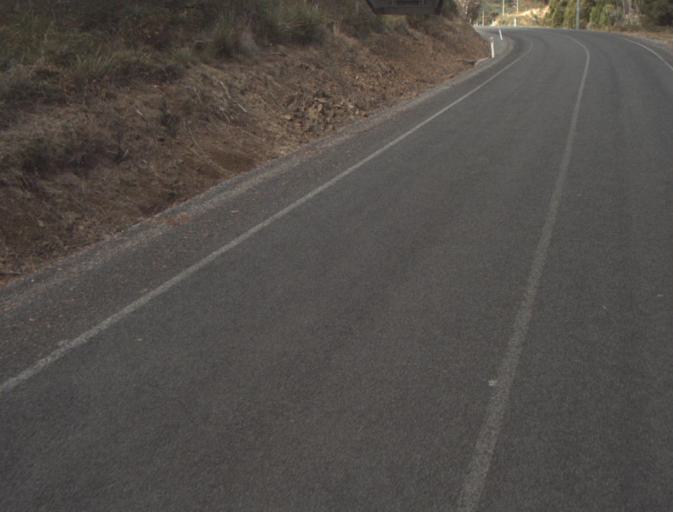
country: AU
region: Tasmania
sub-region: Launceston
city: Mayfield
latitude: -41.3051
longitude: 147.0417
